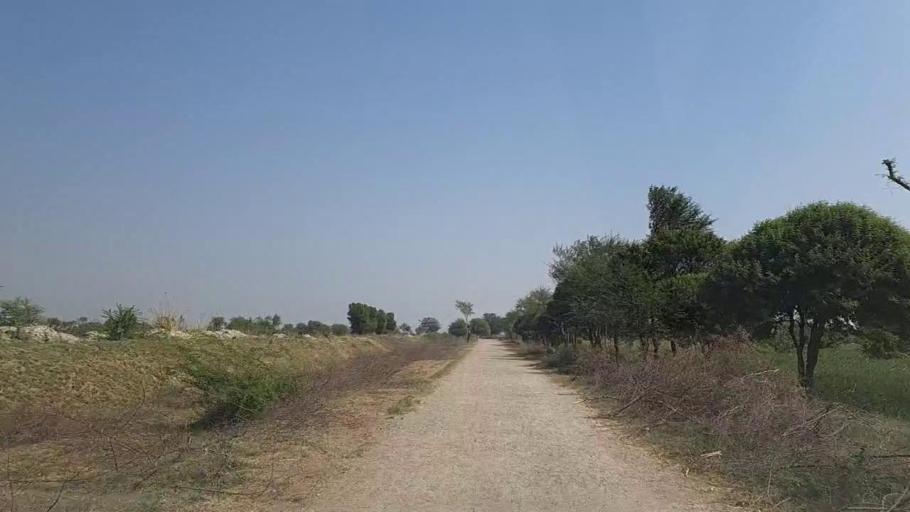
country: PK
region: Sindh
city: Samaro
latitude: 25.2432
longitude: 69.4133
